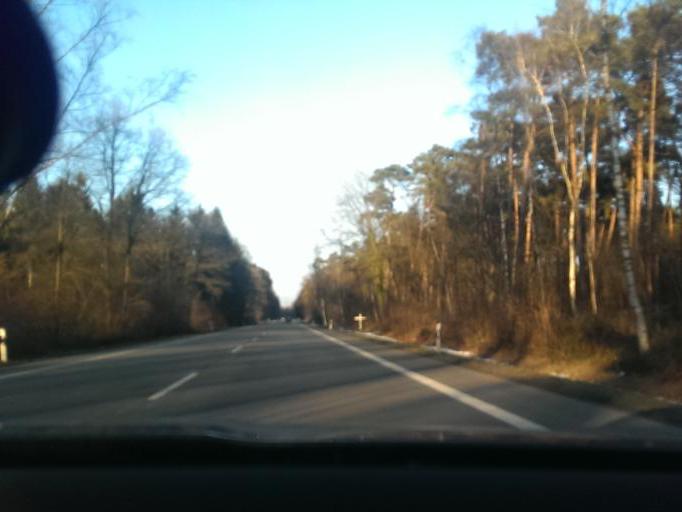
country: DE
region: North Rhine-Westphalia
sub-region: Regierungsbezirk Detmold
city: Hovelhof
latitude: 51.8371
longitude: 8.6615
